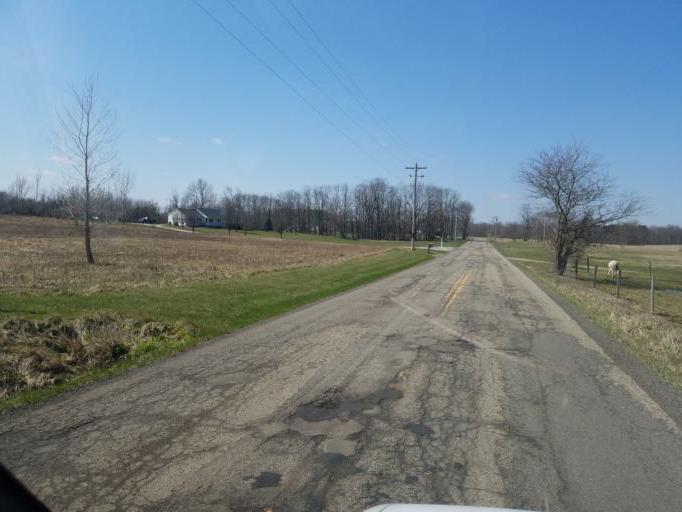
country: US
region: Ohio
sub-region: Knox County
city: Centerburg
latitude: 40.3184
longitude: -82.6319
